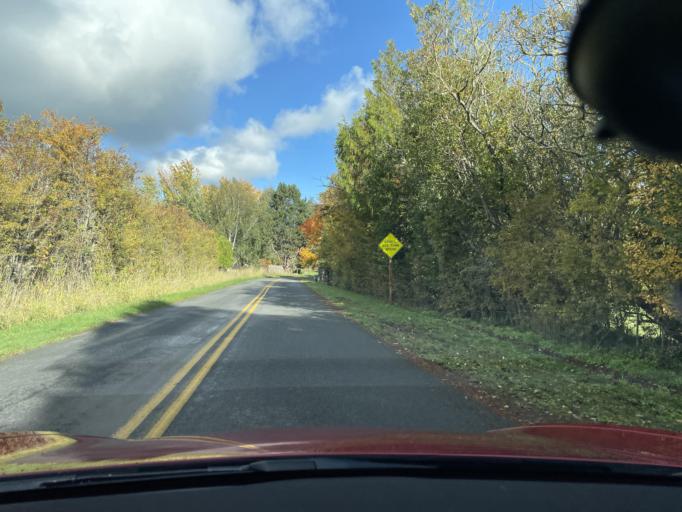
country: US
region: Washington
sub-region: San Juan County
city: Friday Harbor
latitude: 48.5024
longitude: -123.0230
